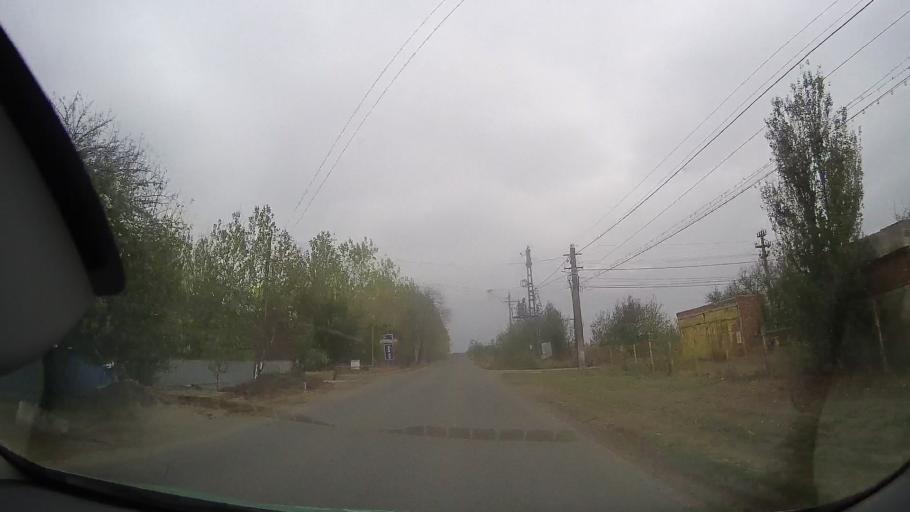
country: RO
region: Buzau
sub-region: Comuna Glodeanu-Silistea
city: Glodeanu-Silistea
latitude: 44.8181
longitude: 26.8400
